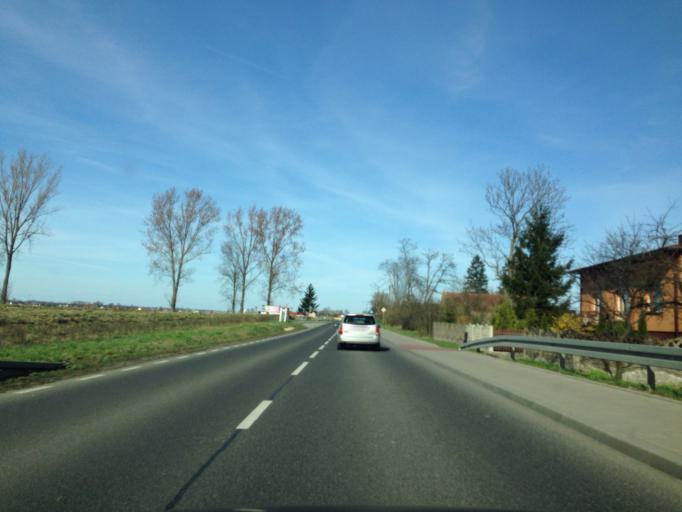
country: PL
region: Lodz Voivodeship
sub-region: Powiat leczycki
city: Leczyca
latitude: 52.0293
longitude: 19.1156
